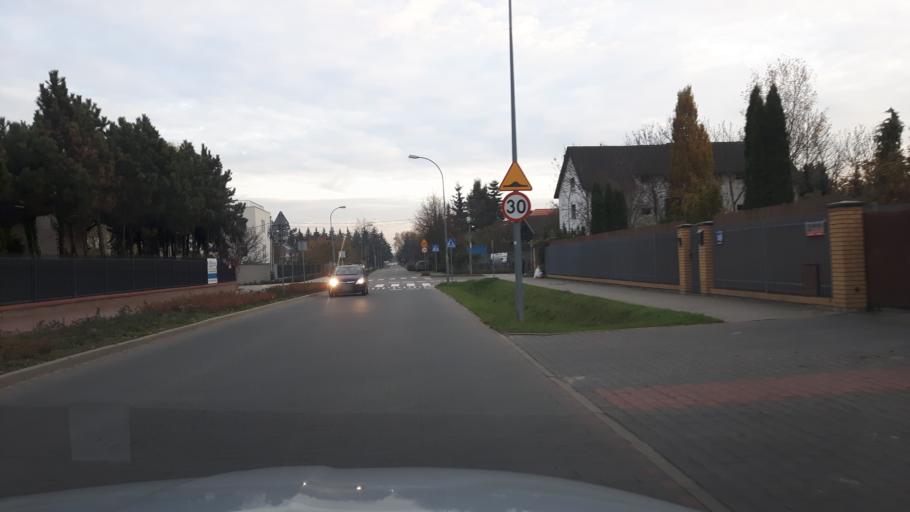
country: PL
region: Masovian Voivodeship
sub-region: Warszawa
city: Wilanow
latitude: 52.1750
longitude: 21.1106
